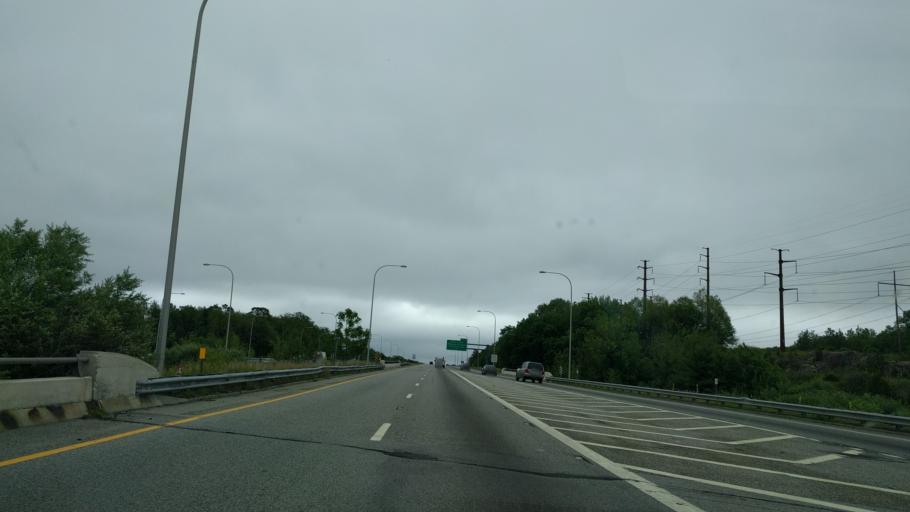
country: US
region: Rhode Island
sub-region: Providence County
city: Johnston
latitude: 41.8203
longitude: -71.5129
